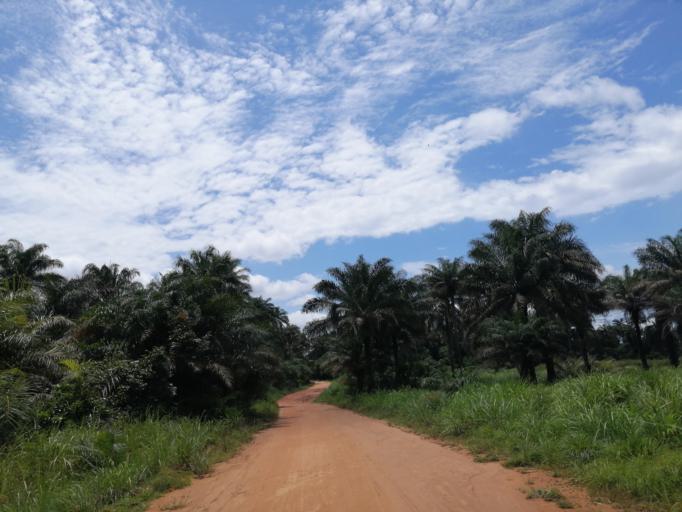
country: SL
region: Northern Province
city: Konakridee
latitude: 8.7510
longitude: -13.1442
